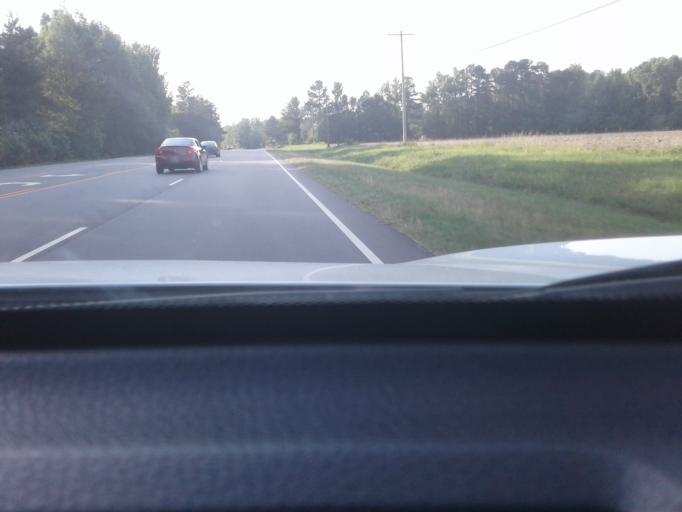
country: US
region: North Carolina
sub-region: Harnett County
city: Buies Creek
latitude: 35.3953
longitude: -78.7309
